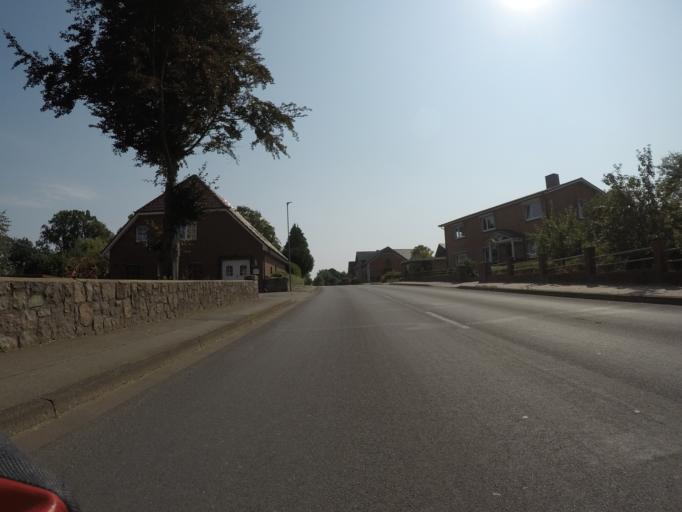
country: DE
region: Schleswig-Holstein
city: Bark
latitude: 53.9093
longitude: 10.1847
